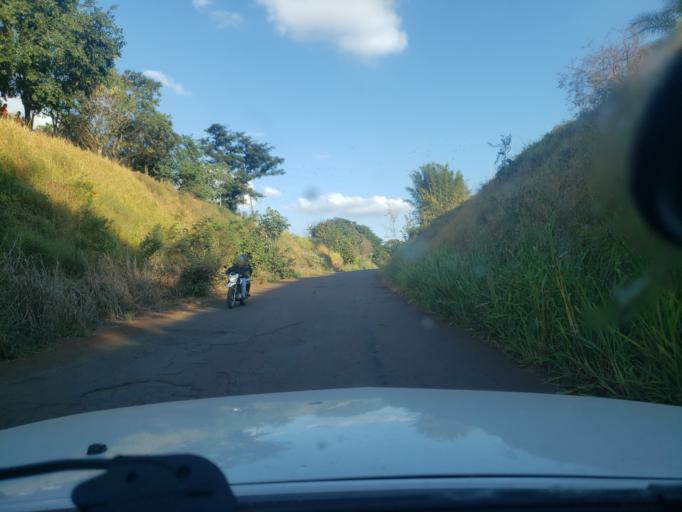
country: BR
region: Sao Paulo
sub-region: Mogi-Mirim
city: Mogi Mirim
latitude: -22.4626
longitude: -46.9341
